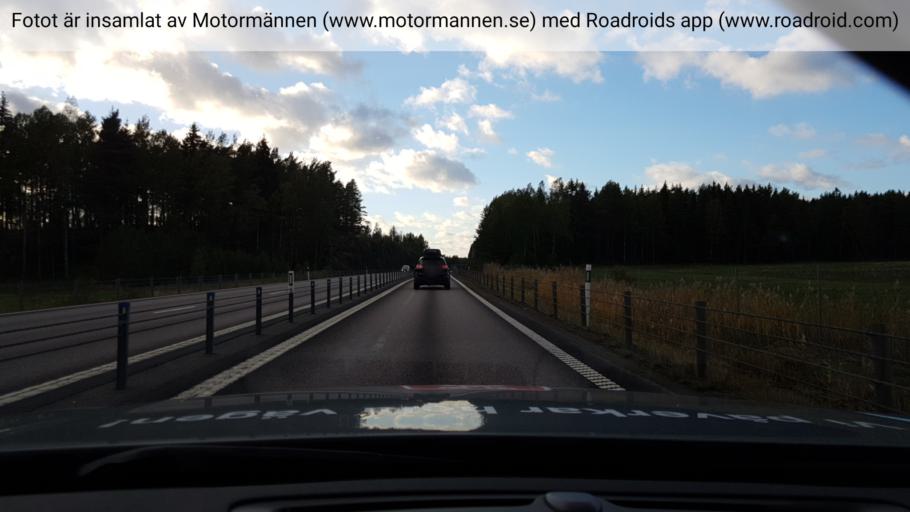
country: SE
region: Vaermland
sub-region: Karlstads Kommun
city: Skattkarr
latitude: 59.4050
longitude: 13.7744
